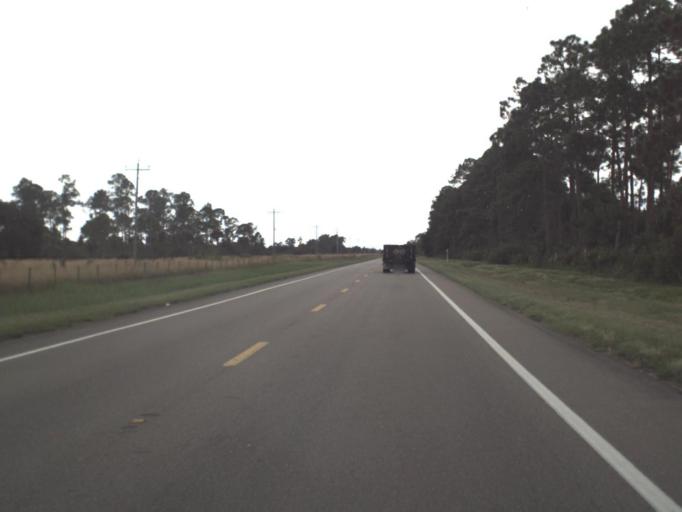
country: US
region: Florida
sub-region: Lee County
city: Olga
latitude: 26.8256
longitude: -81.7601
